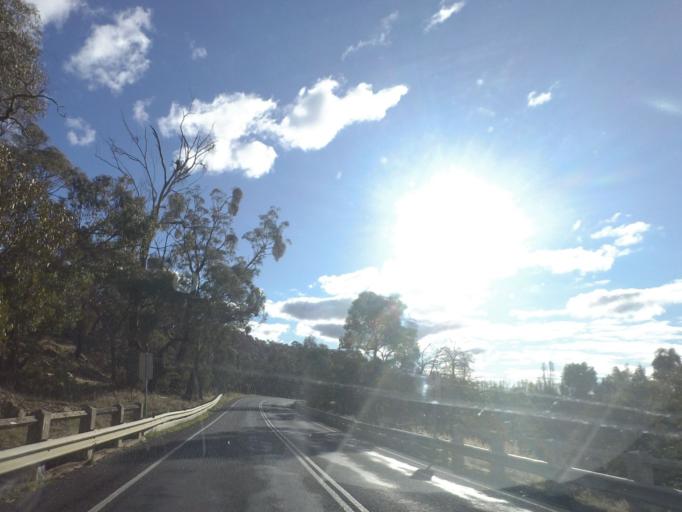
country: AU
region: Victoria
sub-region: Mount Alexander
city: Castlemaine
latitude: -37.1033
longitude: 144.2981
